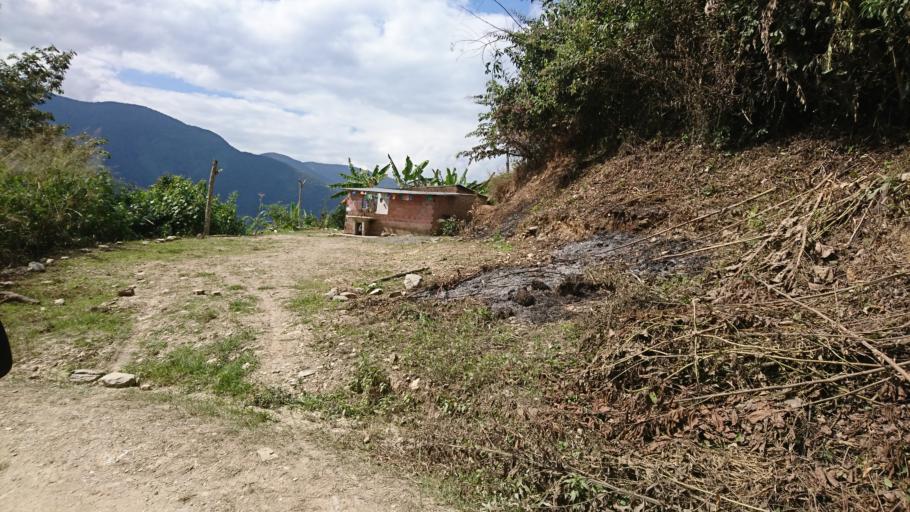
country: BO
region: La Paz
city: Coroico
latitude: -16.0872
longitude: -67.7840
